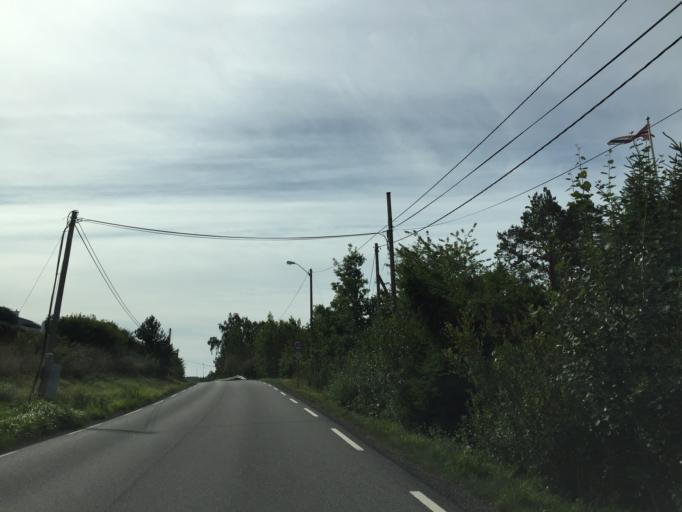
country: NO
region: Ostfold
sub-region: Moss
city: Moss
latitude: 59.5022
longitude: 10.6855
